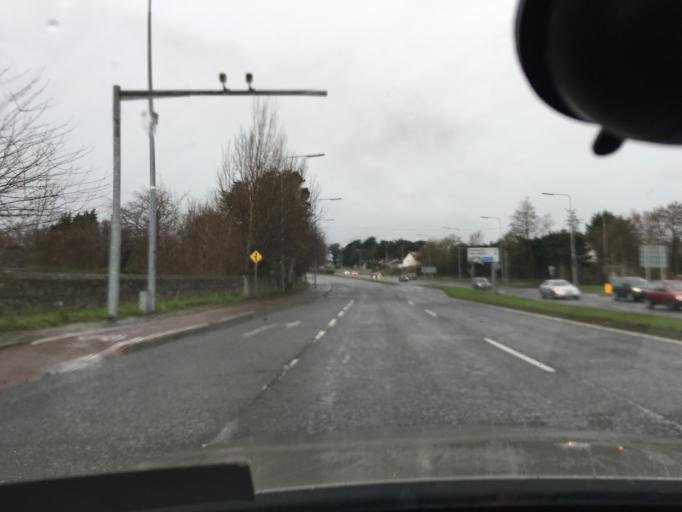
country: IE
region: Leinster
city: Templeogue
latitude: 53.2961
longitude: -6.3100
